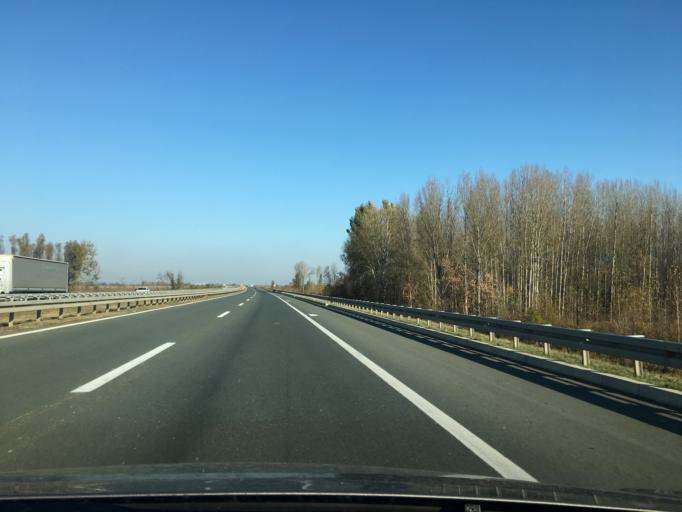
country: RS
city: Beska
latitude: 45.1879
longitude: 20.0769
